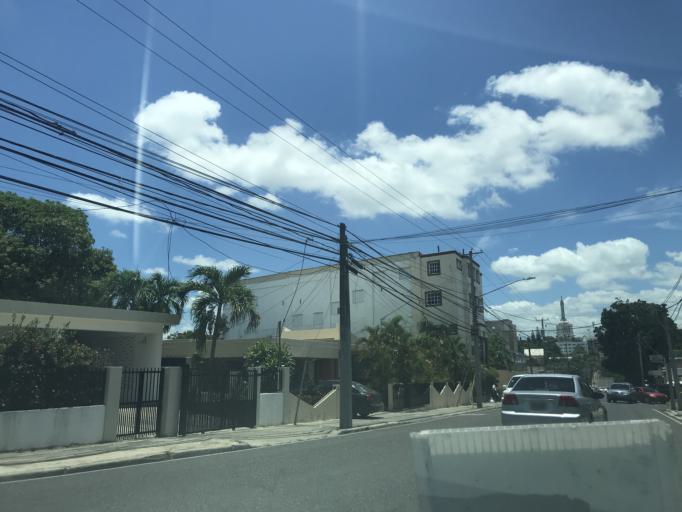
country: DO
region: Santiago
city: Santiago de los Caballeros
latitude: 19.4428
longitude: -70.6988
